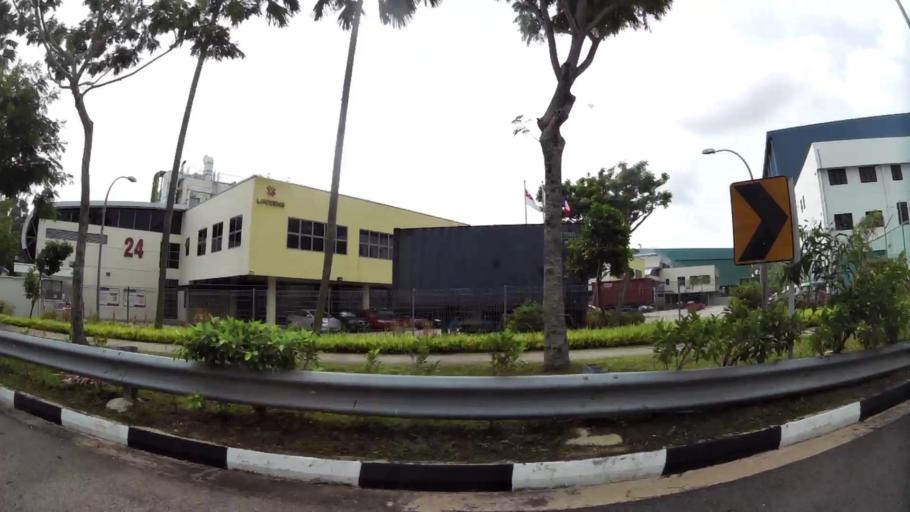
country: SG
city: Singapore
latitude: 1.3521
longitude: 103.9740
